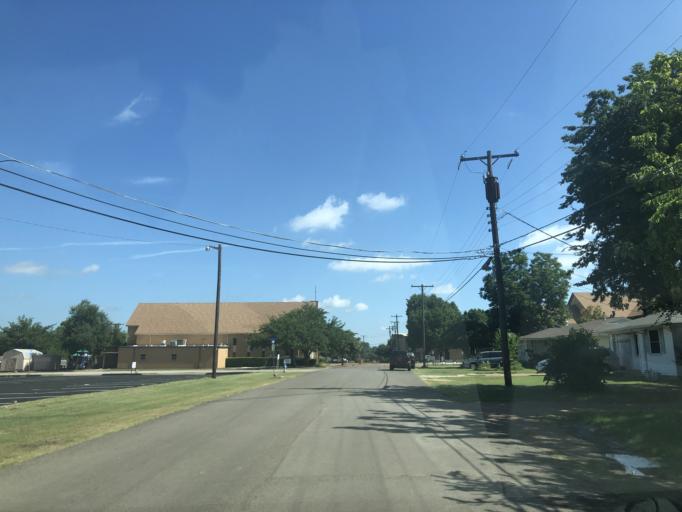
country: US
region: Texas
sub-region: Dallas County
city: Duncanville
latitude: 32.6472
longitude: -96.9098
